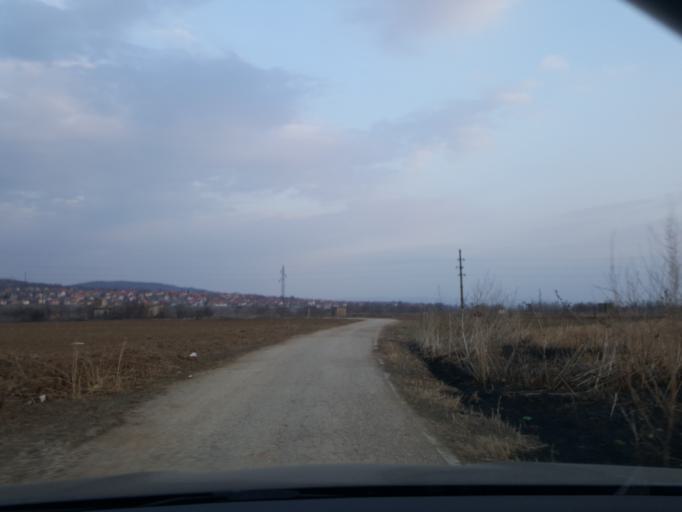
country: RS
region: Central Serbia
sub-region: Nisavski Okrug
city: Aleksinac
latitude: 43.5489
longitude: 21.6763
